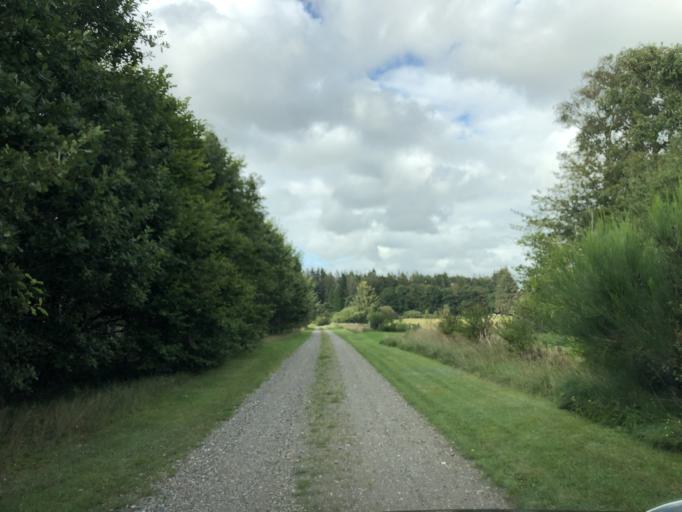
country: DK
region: Central Jutland
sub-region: Holstebro Kommune
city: Ulfborg
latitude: 56.2506
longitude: 8.3877
